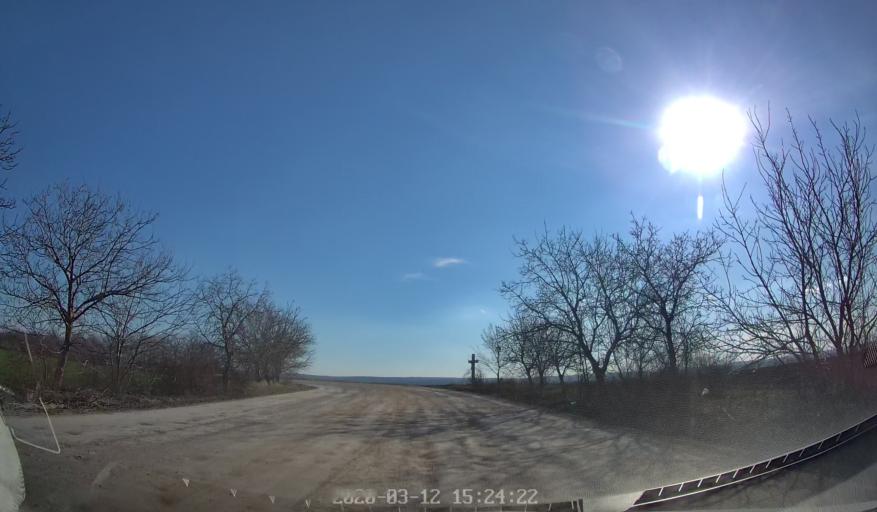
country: MD
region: Chisinau
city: Ciorescu
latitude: 47.1870
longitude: 28.9137
